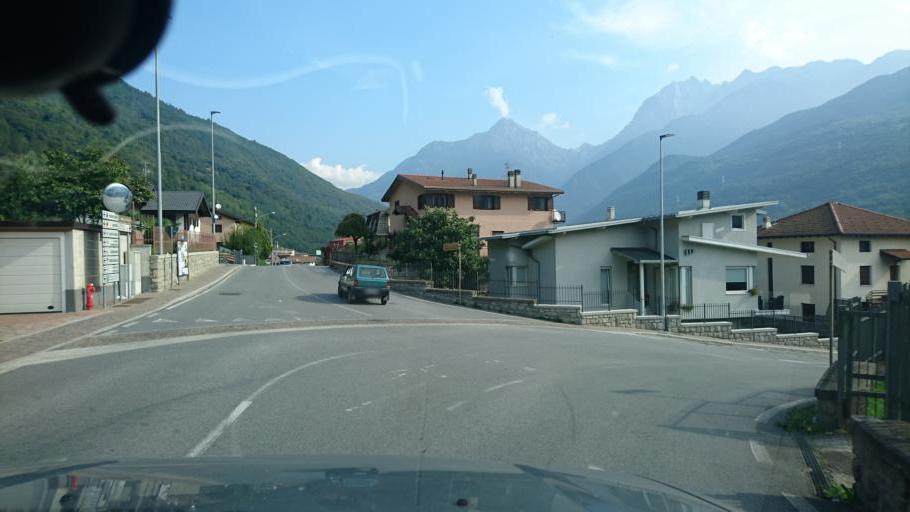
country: IT
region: Lombardy
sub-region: Provincia di Brescia
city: Malonno
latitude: 46.1209
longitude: 10.3173
